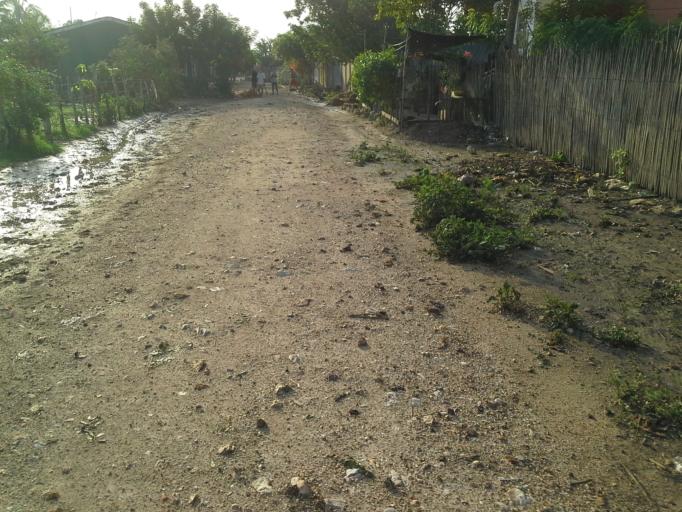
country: CO
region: Cordoba
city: Chima
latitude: 9.1026
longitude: -75.6281
